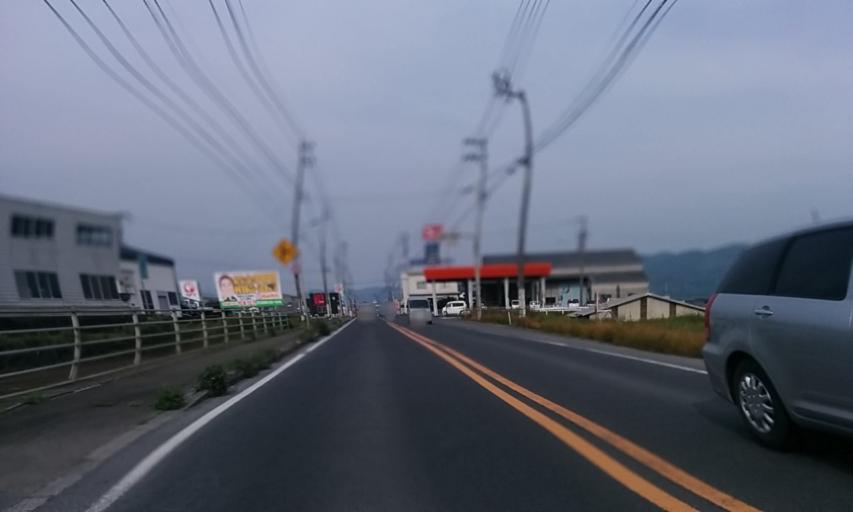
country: JP
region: Ehime
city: Niihama
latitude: 33.9581
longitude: 133.4389
